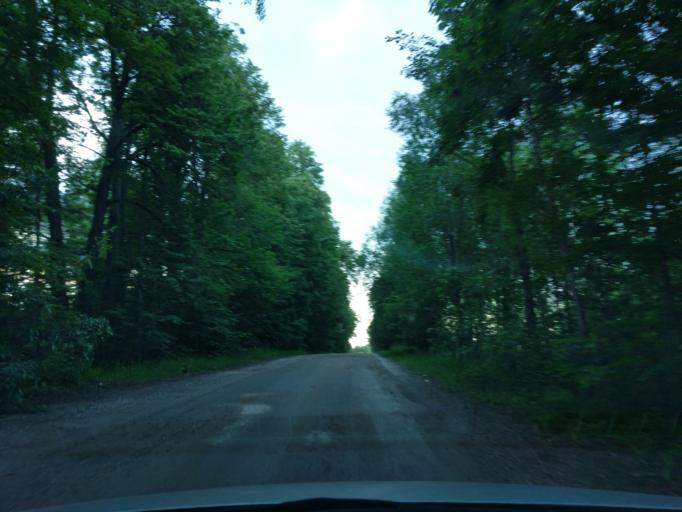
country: RU
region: Kaluga
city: Myatlevo
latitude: 54.8627
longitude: 35.5696
